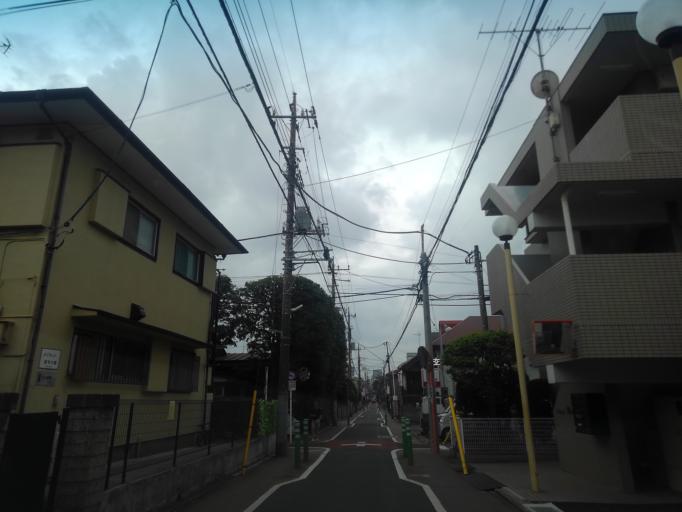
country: JP
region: Tokyo
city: Musashino
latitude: 35.7111
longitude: 139.5864
